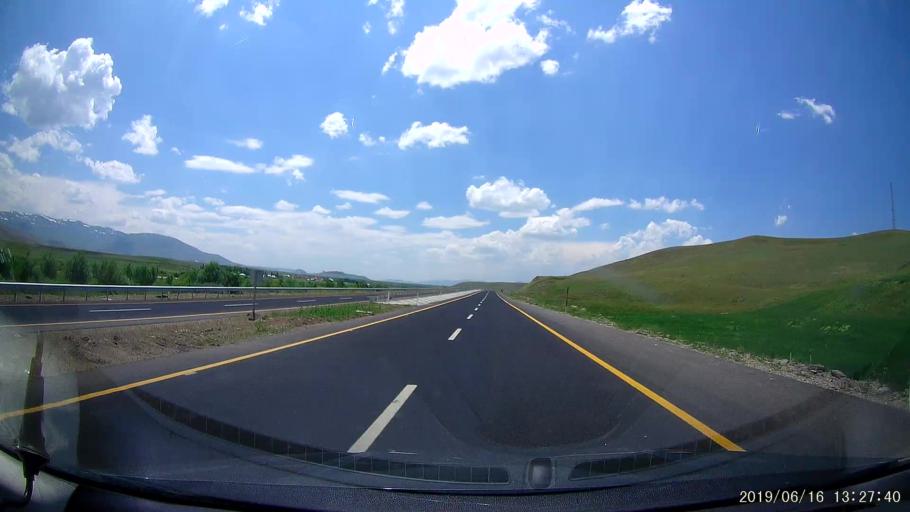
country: TR
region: Agri
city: Murat
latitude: 39.6717
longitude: 43.3051
